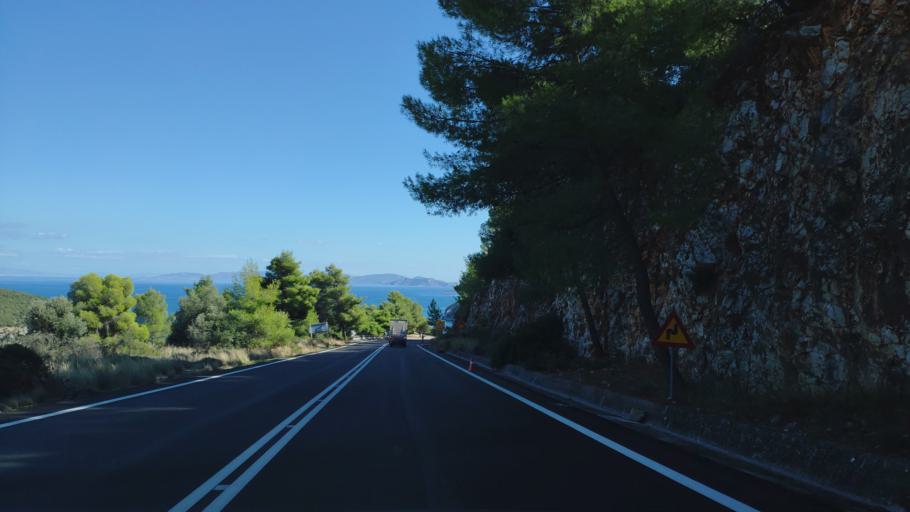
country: GR
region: Peloponnese
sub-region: Nomos Korinthias
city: Sofikon
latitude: 37.7309
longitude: 23.1149
